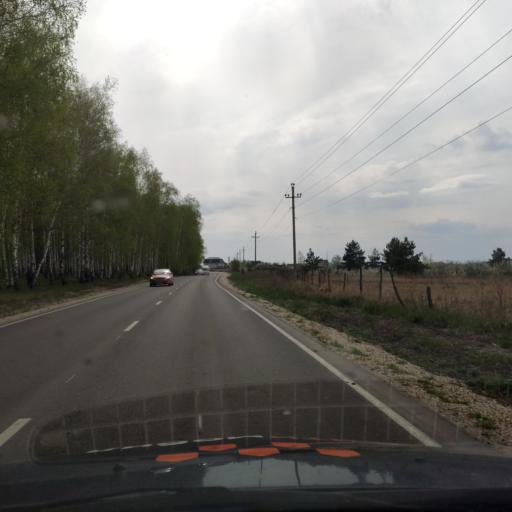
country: RU
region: Voronezj
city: Podgornoye
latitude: 51.8422
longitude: 39.1442
